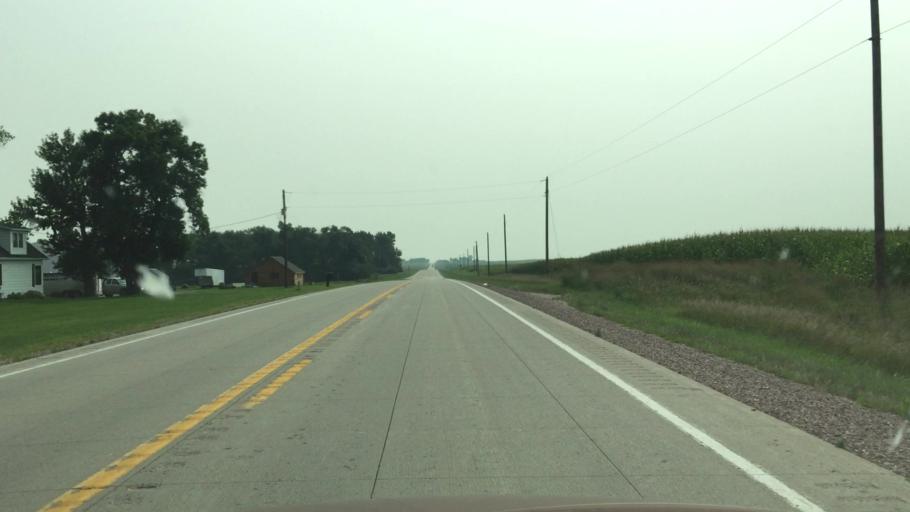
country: US
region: Iowa
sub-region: Osceola County
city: Sibley
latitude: 43.4327
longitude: -95.6964
